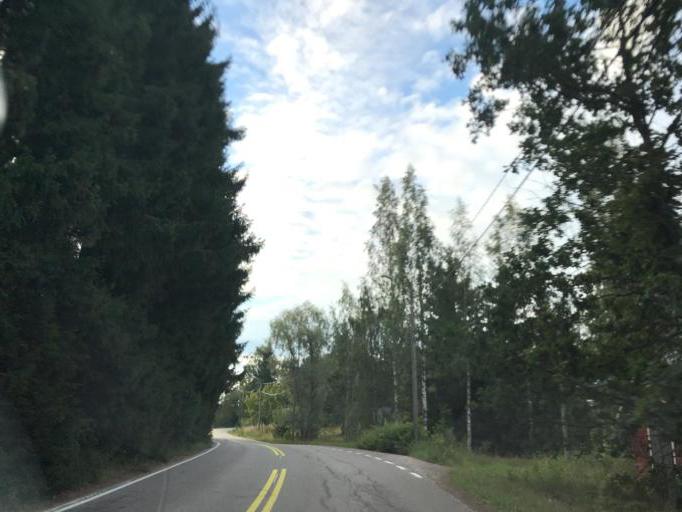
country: FI
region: Uusimaa
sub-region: Helsinki
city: Vihti
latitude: 60.3873
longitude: 24.5200
